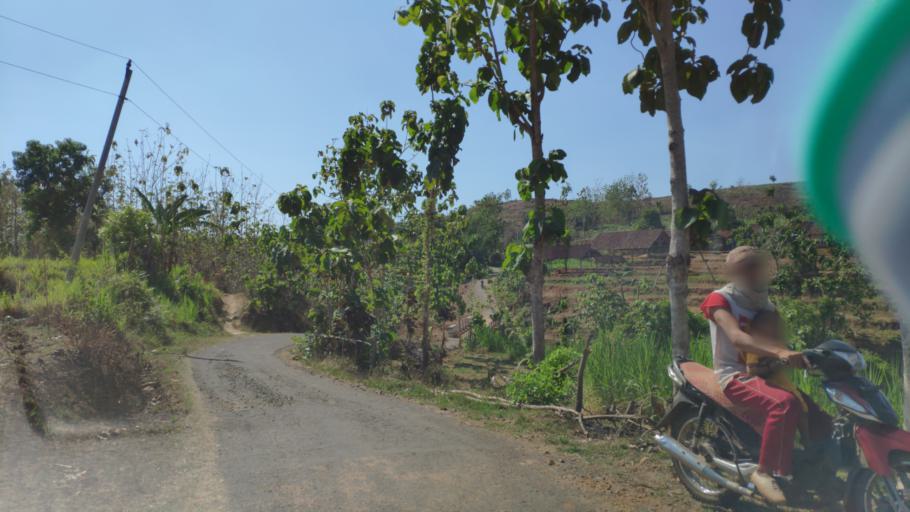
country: ID
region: East Java
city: Krajan Jamprong
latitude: -6.9814
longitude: 111.6206
